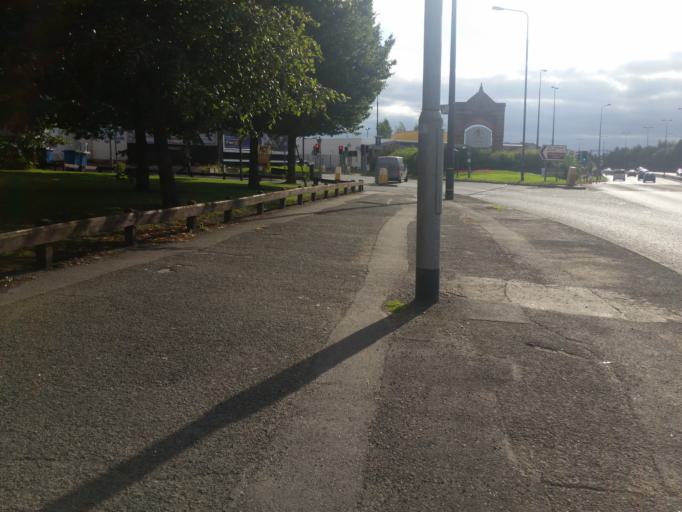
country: GB
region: England
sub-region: Manchester
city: Hulme
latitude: 53.4697
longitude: -2.2651
